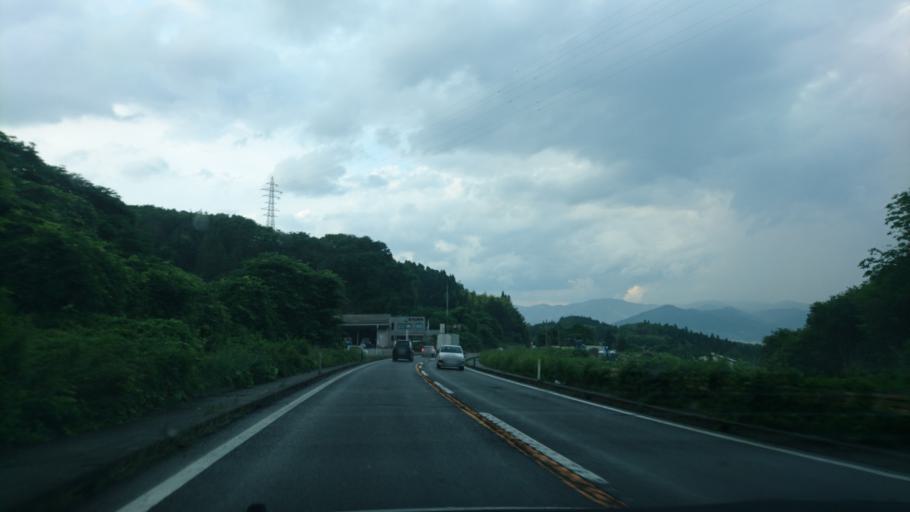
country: JP
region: Iwate
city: Ichinoseki
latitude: 38.9484
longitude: 141.1184
